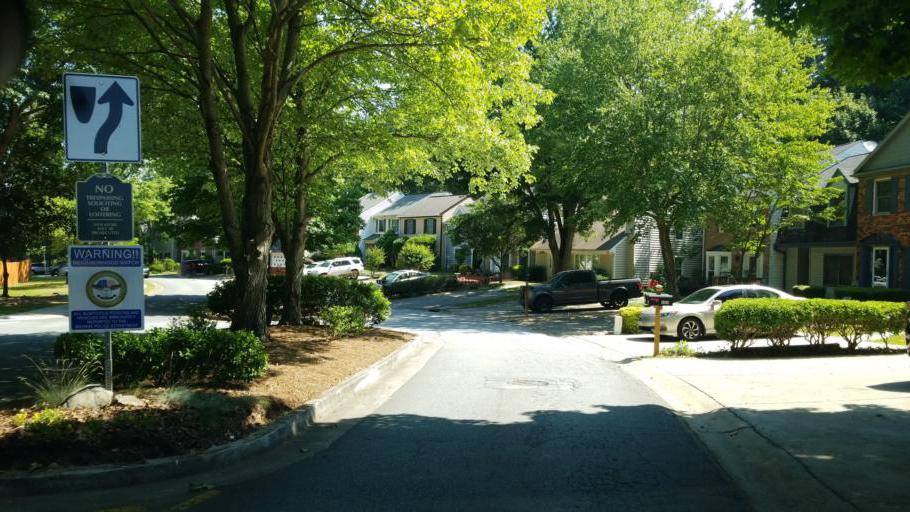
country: US
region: Georgia
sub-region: Cobb County
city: Vinings
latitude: 33.8869
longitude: -84.4800
